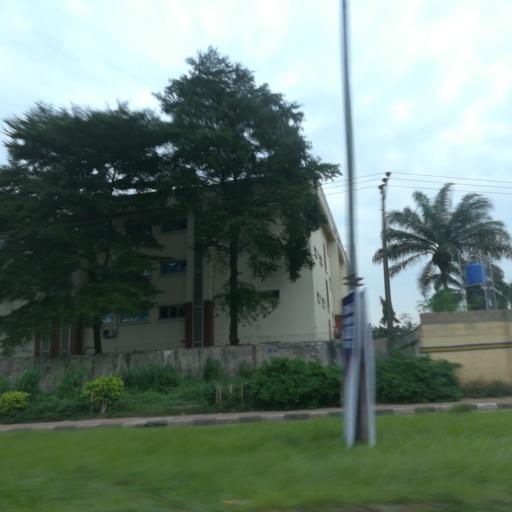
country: NG
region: Lagos
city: Ikeja
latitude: 6.5897
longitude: 3.3551
